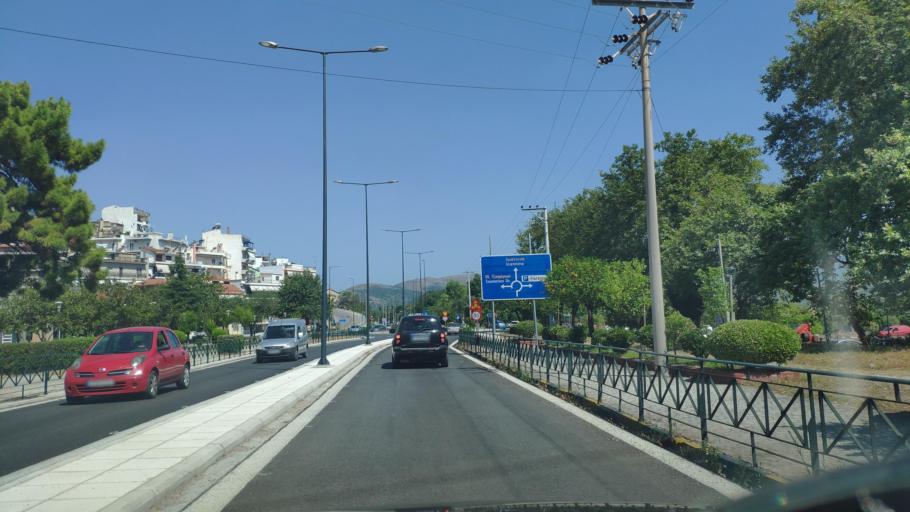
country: GR
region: Epirus
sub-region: Nomos Artas
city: Arta
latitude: 39.1612
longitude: 20.9941
